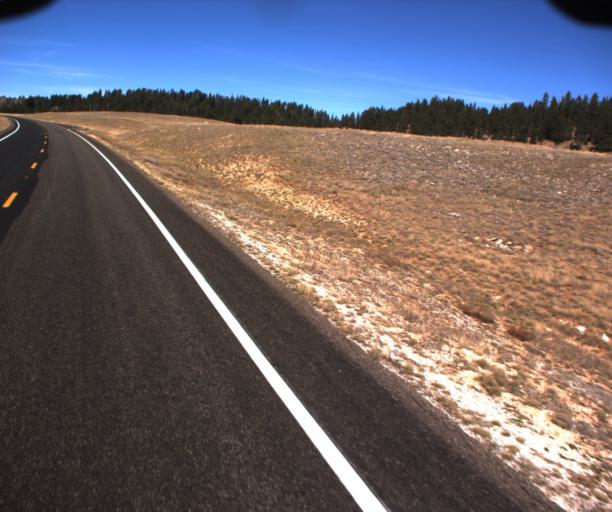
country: US
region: Arizona
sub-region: Coconino County
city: Grand Canyon
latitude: 36.4948
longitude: -112.1320
